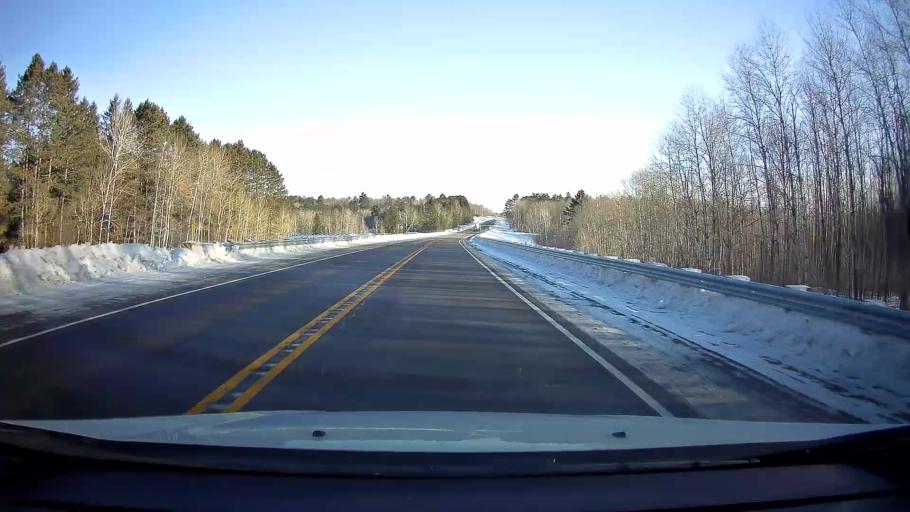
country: US
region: Wisconsin
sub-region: Sawyer County
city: Hayward
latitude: 46.0681
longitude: -91.4338
